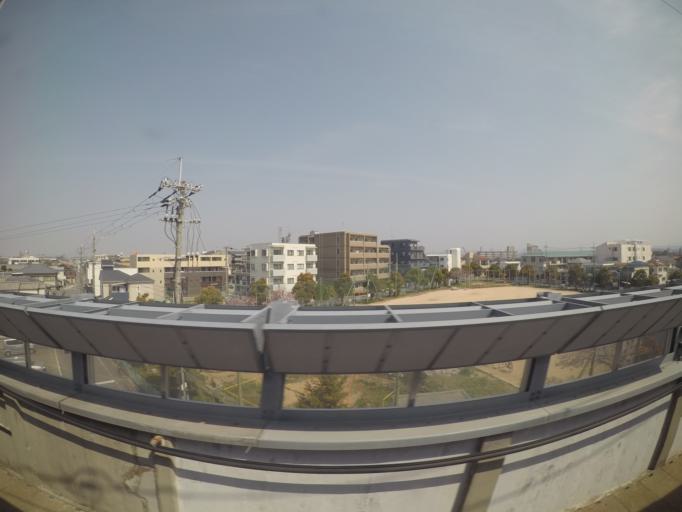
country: JP
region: Hyogo
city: Akashi
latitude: 34.6664
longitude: 134.9695
